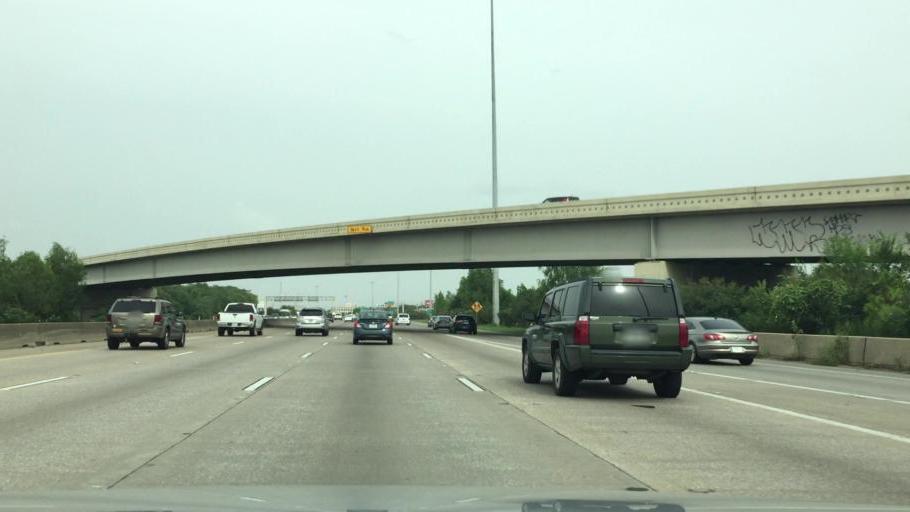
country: US
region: Texas
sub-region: Harris County
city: Jacinto City
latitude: 29.7747
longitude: -95.2588
